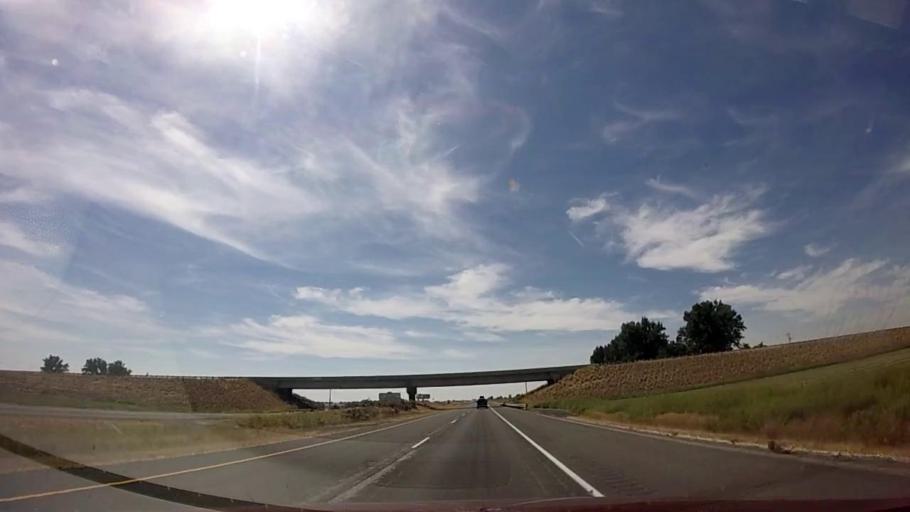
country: US
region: Idaho
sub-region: Minidoka County
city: Rupert
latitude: 42.5690
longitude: -113.7045
